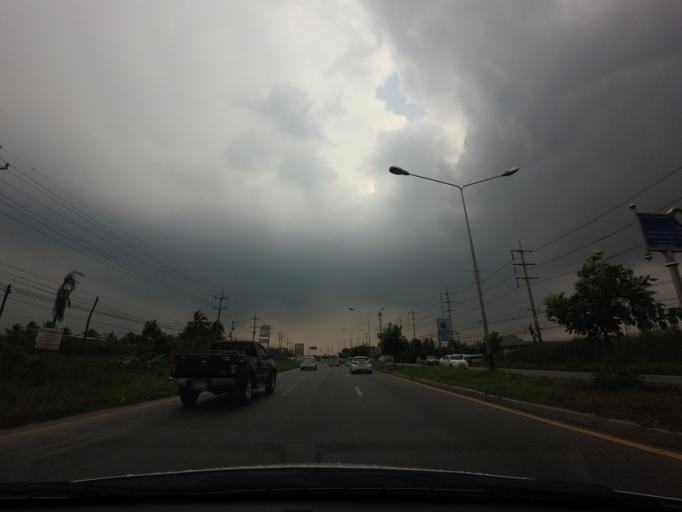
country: TH
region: Nakhon Pathom
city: Salaya
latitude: 13.7849
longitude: 100.2551
